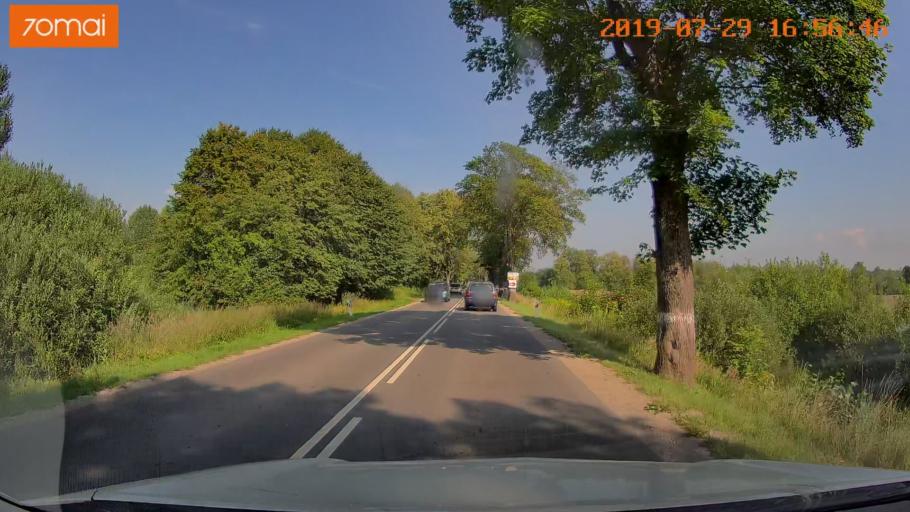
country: RU
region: Kaliningrad
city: Volochayevskoye
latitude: 54.8147
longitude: 20.1757
